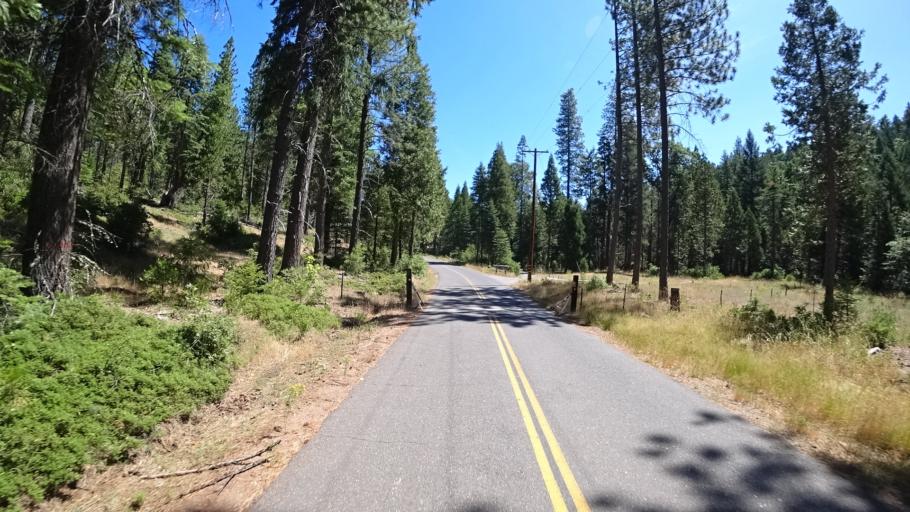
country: US
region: California
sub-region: Amador County
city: Pioneer
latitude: 38.4372
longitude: -120.4344
